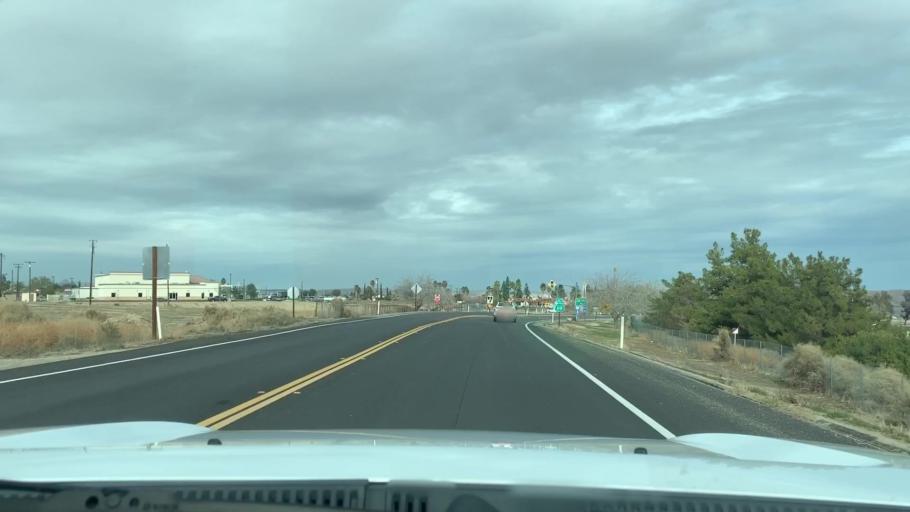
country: US
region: California
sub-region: Kern County
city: South Taft
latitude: 35.1339
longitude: -119.4472
